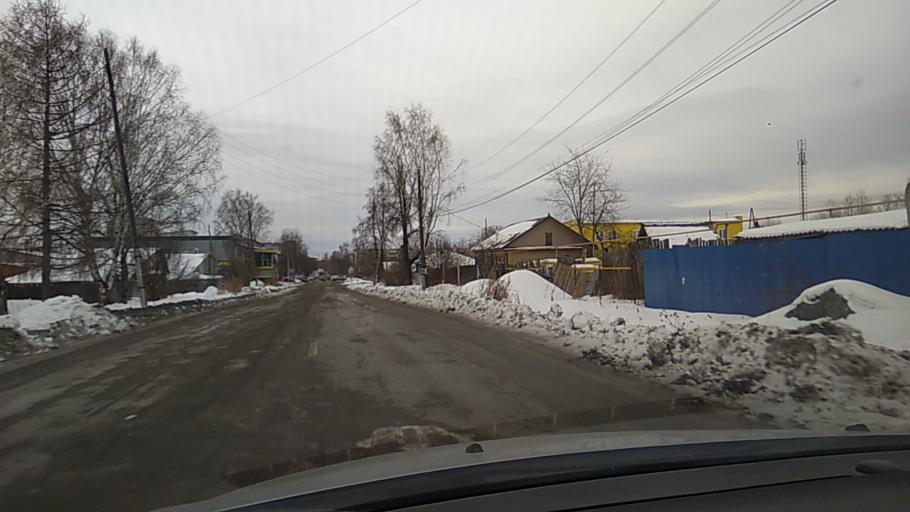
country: RU
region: Sverdlovsk
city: Revda
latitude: 56.8077
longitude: 59.9357
